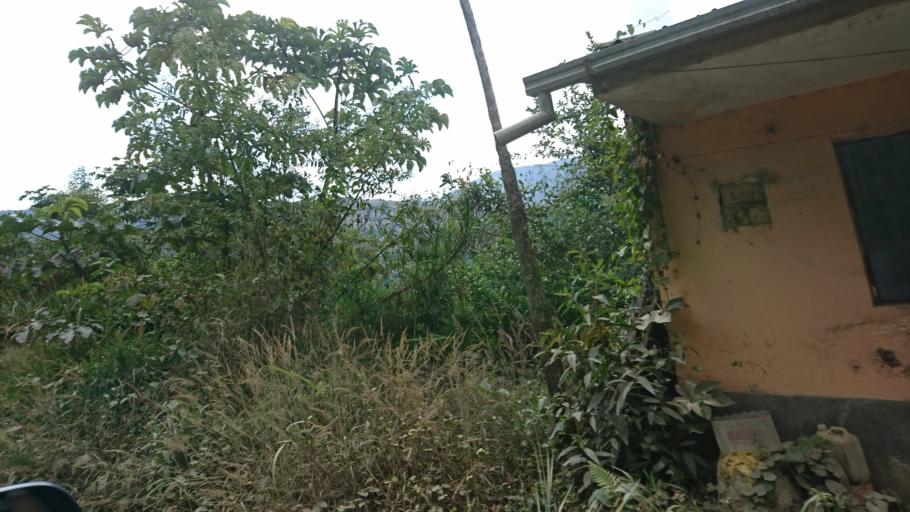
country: BO
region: La Paz
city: Coroico
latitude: -16.0853
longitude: -67.7856
